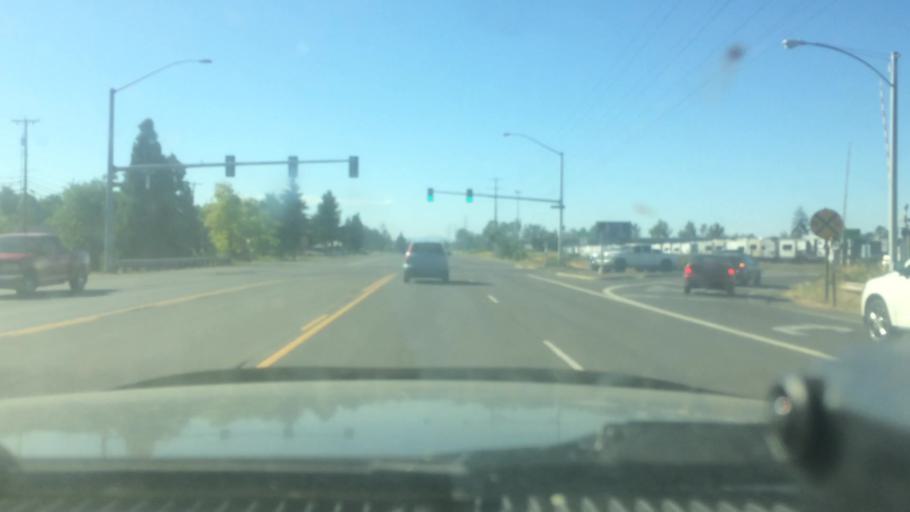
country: US
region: Oregon
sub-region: Lane County
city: Eugene
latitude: 44.0883
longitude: -123.1581
